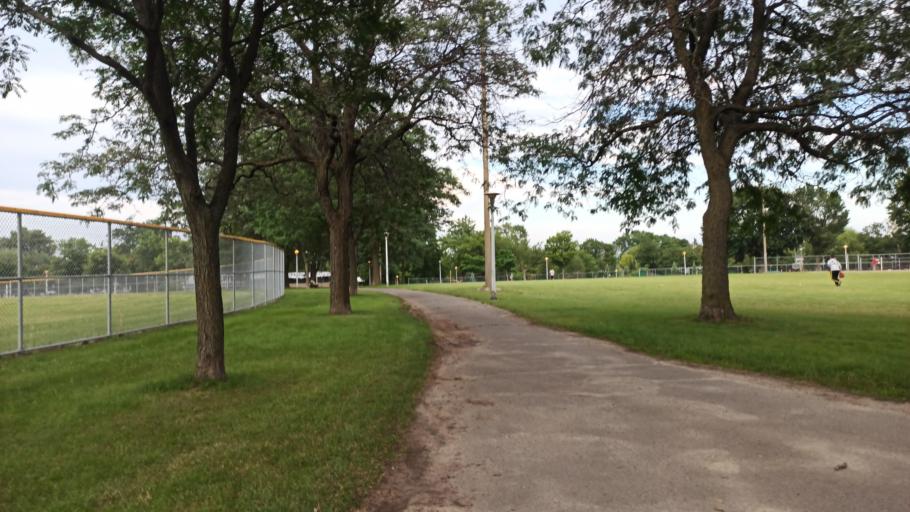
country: CA
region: Quebec
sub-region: Montreal
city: Saint-Leonard
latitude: 45.5690
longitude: -73.5731
